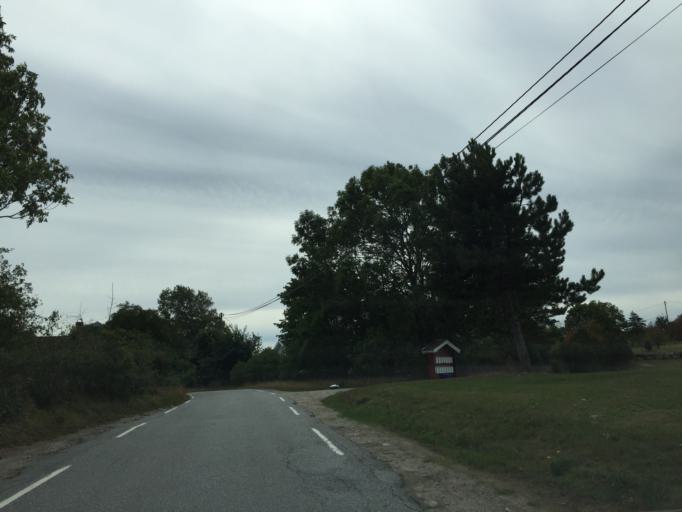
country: NO
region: Ostfold
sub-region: Hvaler
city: Skjaerhalden
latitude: 59.0429
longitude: 10.9537
